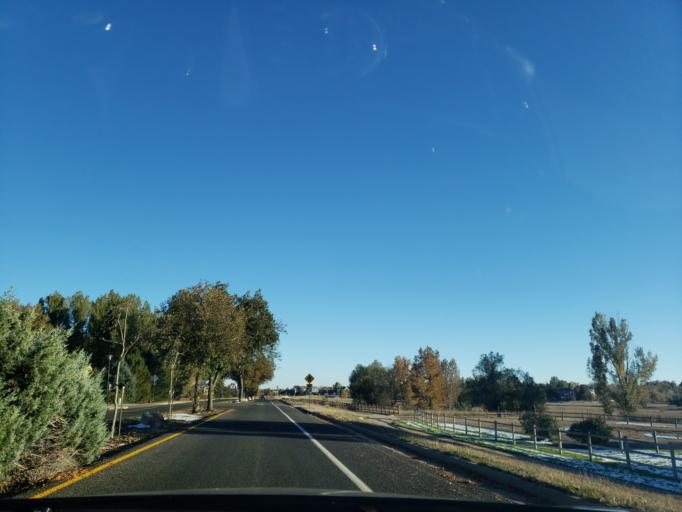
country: US
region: Colorado
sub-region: Larimer County
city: Fort Collins
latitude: 40.5123
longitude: -105.0714
